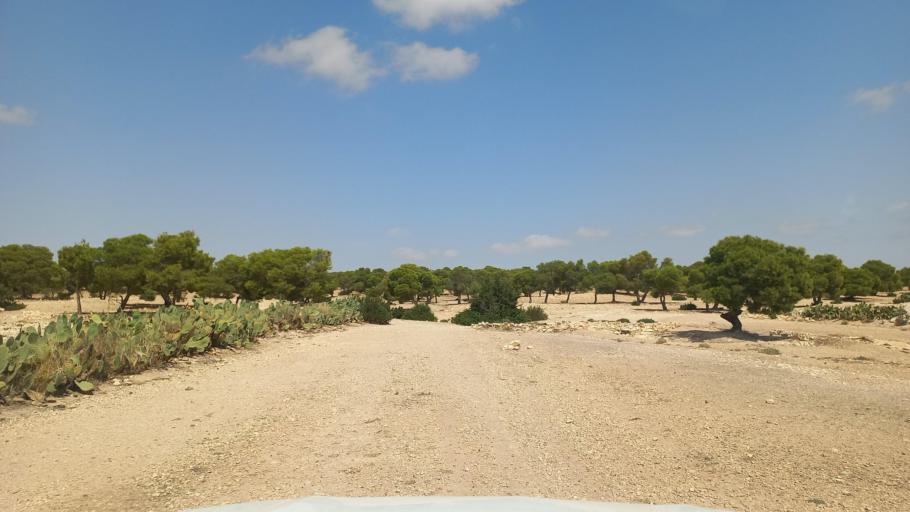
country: TN
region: Al Qasrayn
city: Sbiba
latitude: 35.4054
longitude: 8.9698
